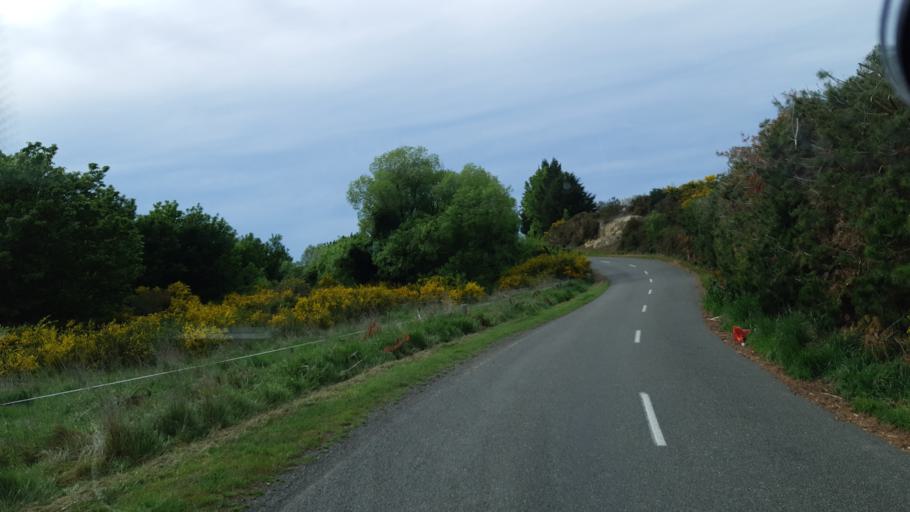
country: NZ
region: Canterbury
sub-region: Timaru District
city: Timaru
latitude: -44.5446
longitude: 171.1729
